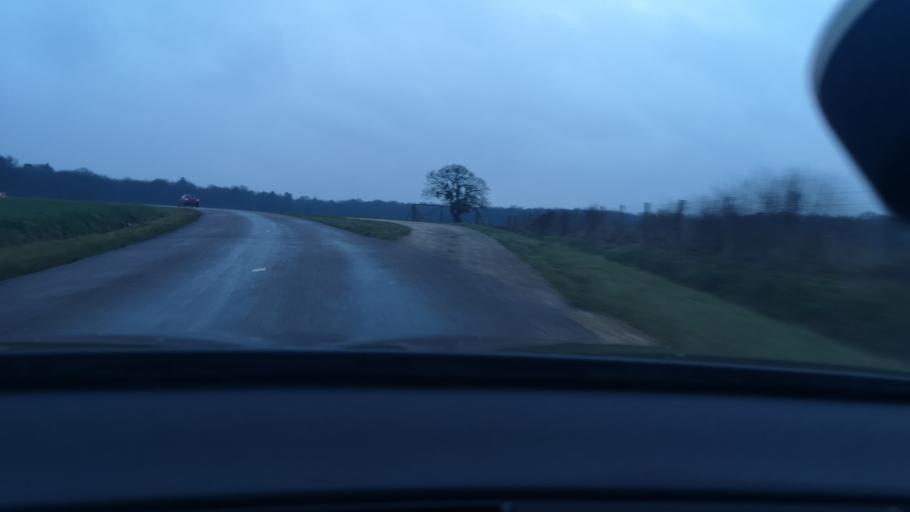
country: FR
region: Bourgogne
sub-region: Departement de la Cote-d'Or
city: Seurre
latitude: 47.0263
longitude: 5.0607
